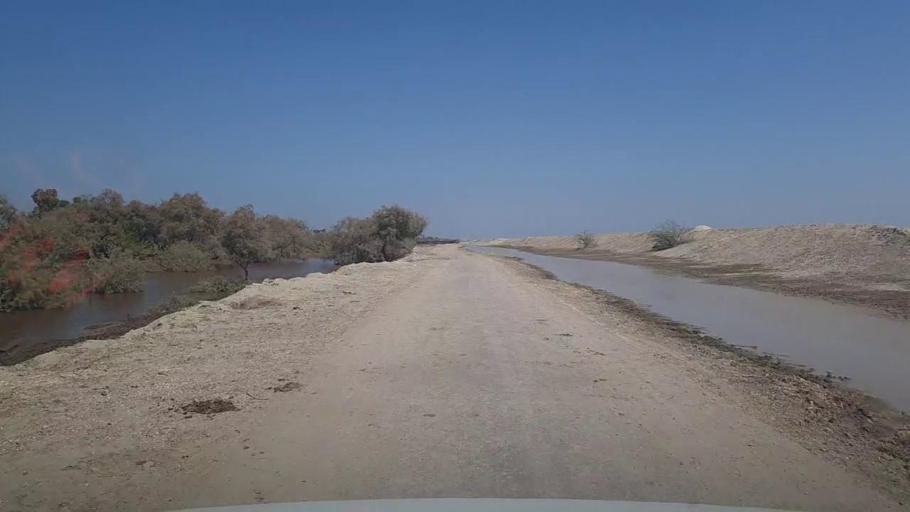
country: PK
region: Sindh
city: Kashmor
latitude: 28.2826
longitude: 69.4589
